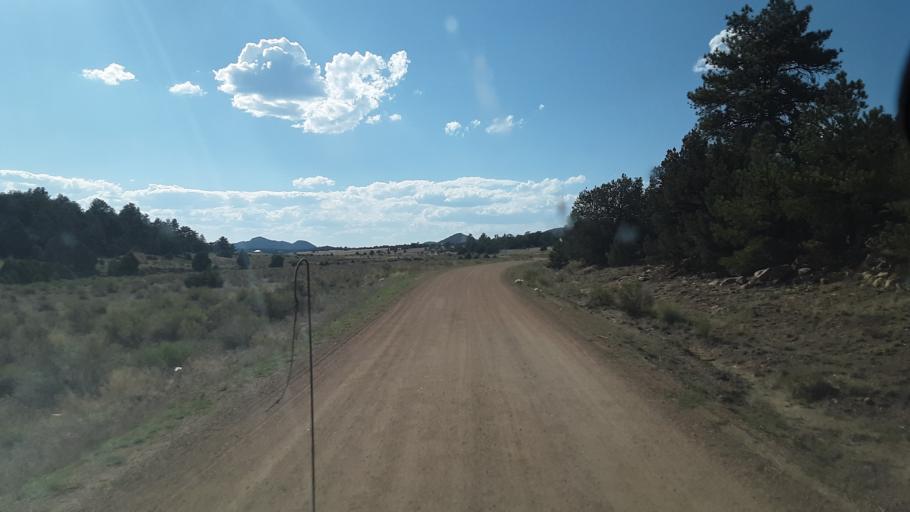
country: US
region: Colorado
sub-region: Custer County
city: Westcliffe
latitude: 38.2814
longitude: -105.4703
